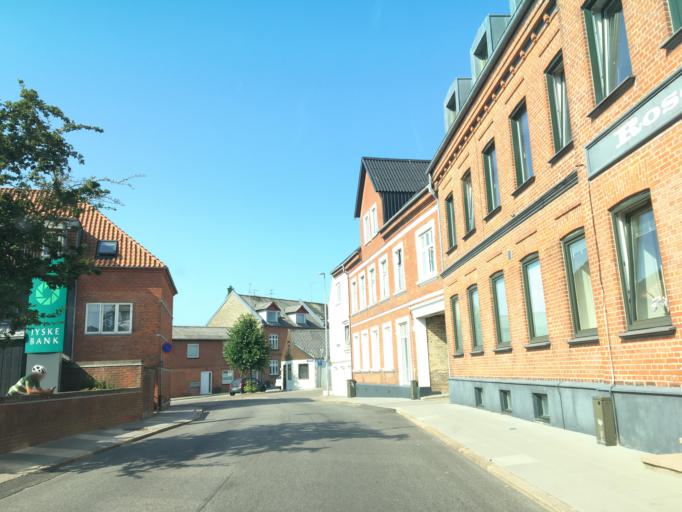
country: DK
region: North Denmark
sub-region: Thisted Kommune
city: Thisted
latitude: 56.9549
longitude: 8.6856
